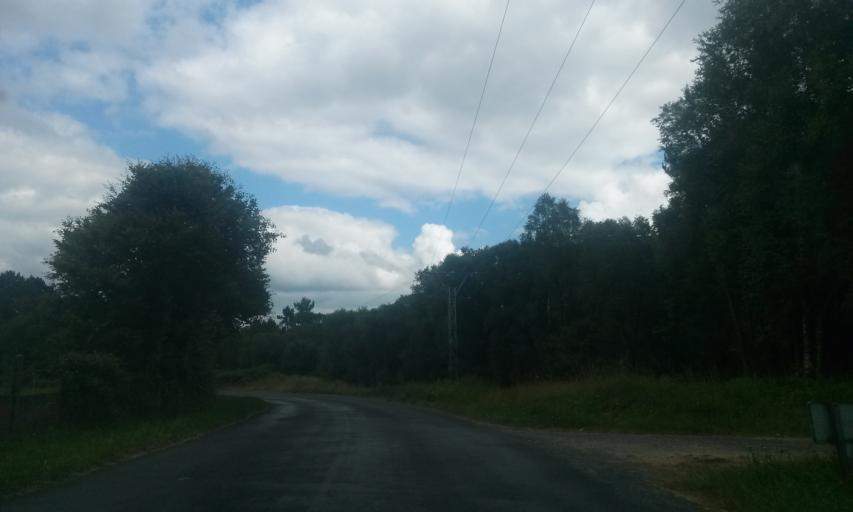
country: ES
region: Galicia
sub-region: Provincia de Lugo
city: Outeiro de Rei
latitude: 43.0608
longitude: -7.6085
